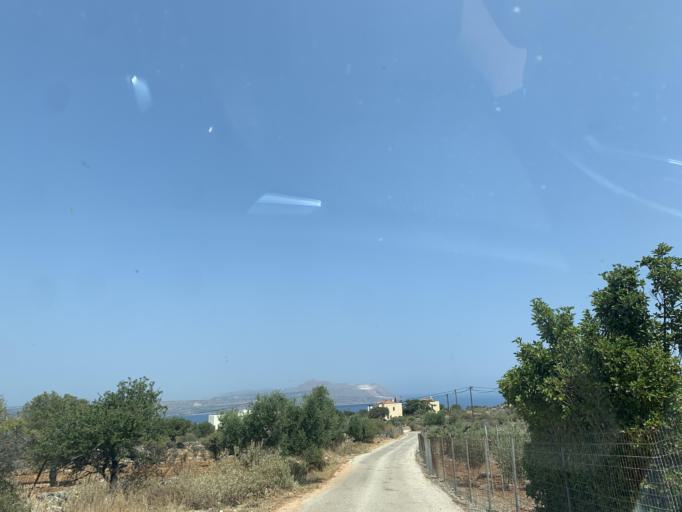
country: GR
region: Crete
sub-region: Nomos Chanias
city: Kalivai
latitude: 35.4516
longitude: 24.2341
